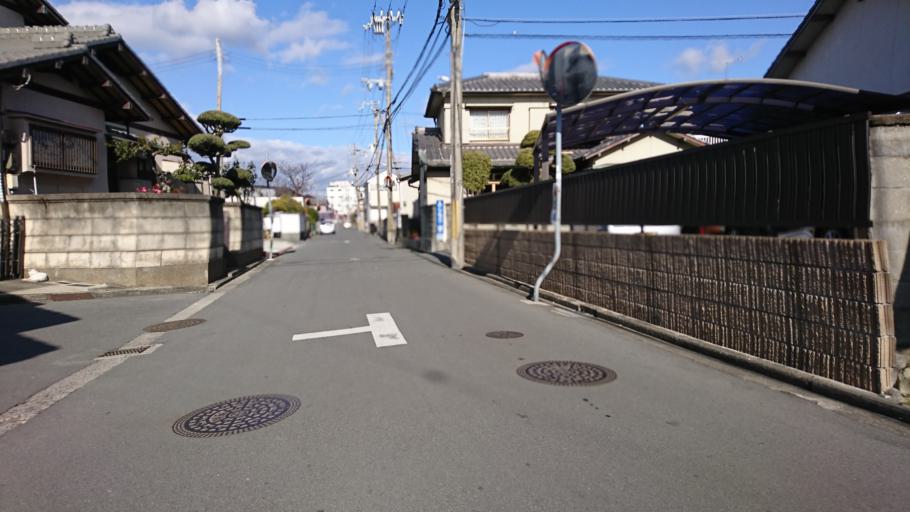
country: JP
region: Hyogo
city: Kakogawacho-honmachi
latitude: 34.7733
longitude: 134.7734
